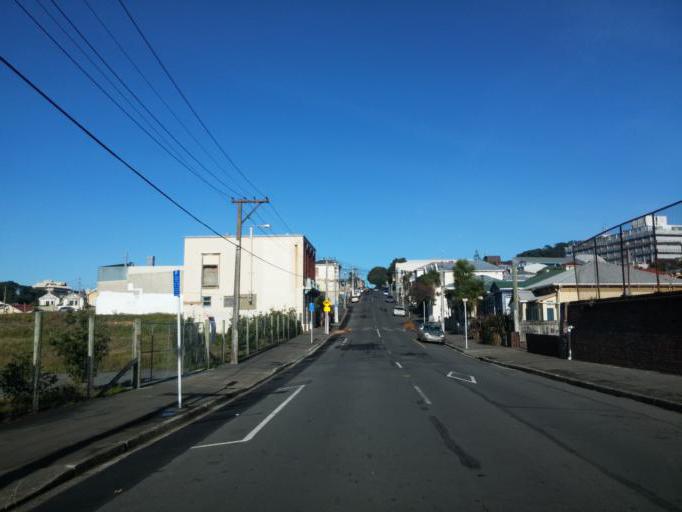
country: NZ
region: Wellington
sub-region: Wellington City
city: Wellington
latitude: -41.3008
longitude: 174.7777
